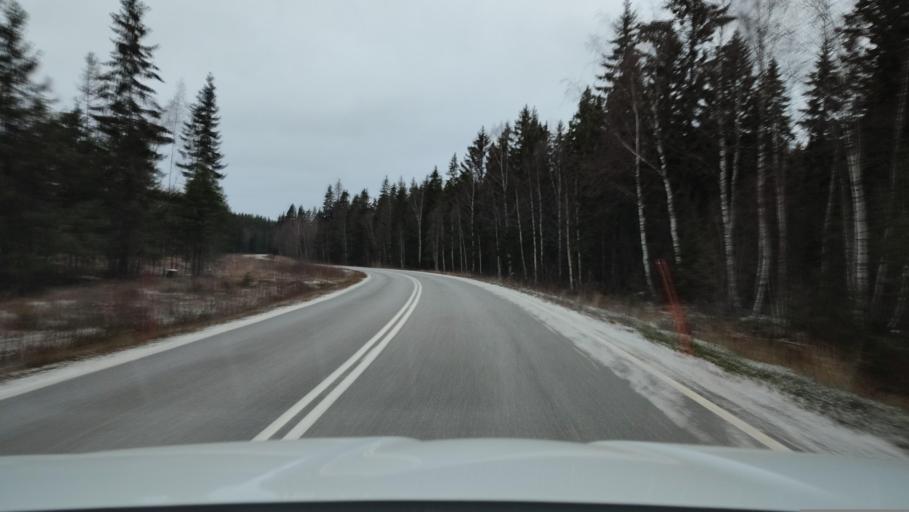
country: FI
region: Ostrobothnia
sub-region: Vaasa
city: Replot
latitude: 63.2650
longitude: 21.3570
